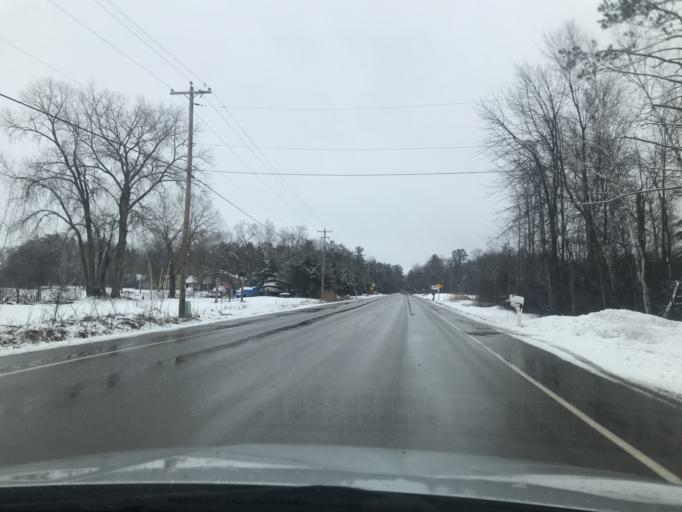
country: US
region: Wisconsin
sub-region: Marinette County
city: Marinette
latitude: 45.1117
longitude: -87.6714
